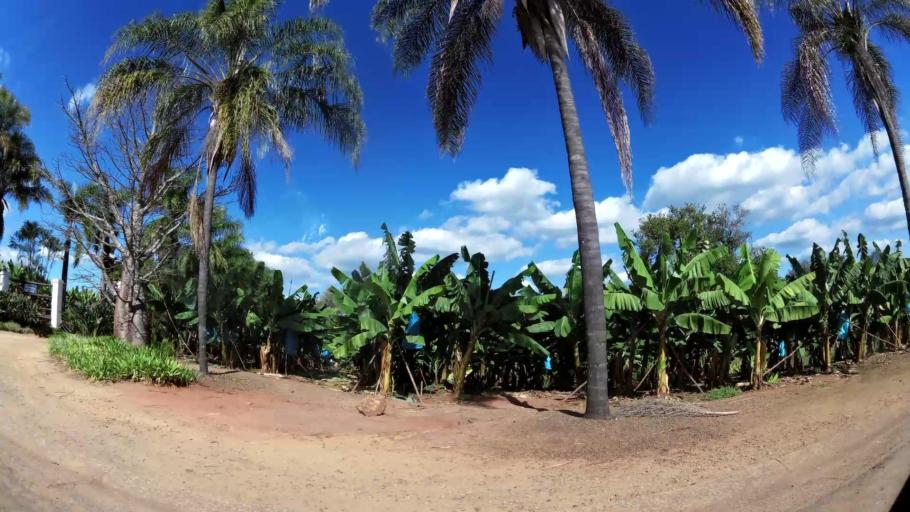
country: ZA
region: Limpopo
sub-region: Mopani District Municipality
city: Tzaneen
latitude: -23.8026
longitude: 30.1279
